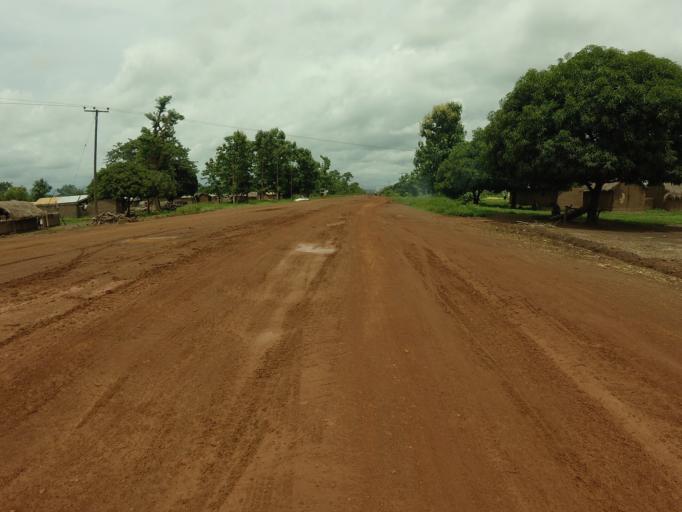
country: GH
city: Kpandae
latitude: 8.4139
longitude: 0.3918
